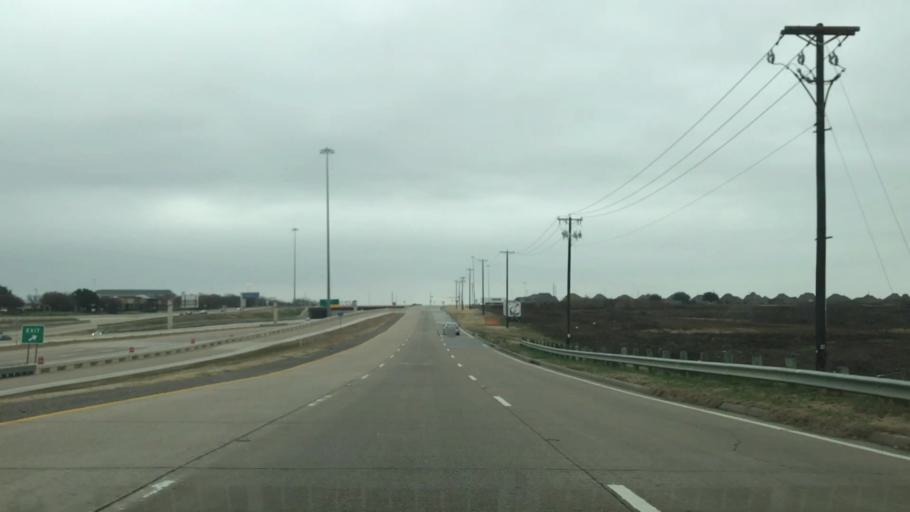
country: US
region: Texas
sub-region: Dallas County
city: Farmers Branch
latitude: 32.9049
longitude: -96.9572
